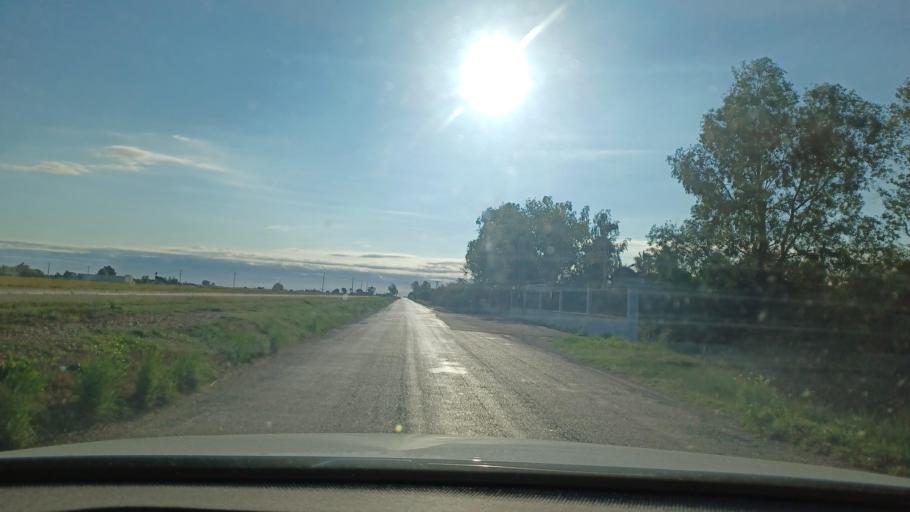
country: ES
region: Catalonia
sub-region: Provincia de Tarragona
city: Amposta
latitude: 40.7008
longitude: 0.6024
